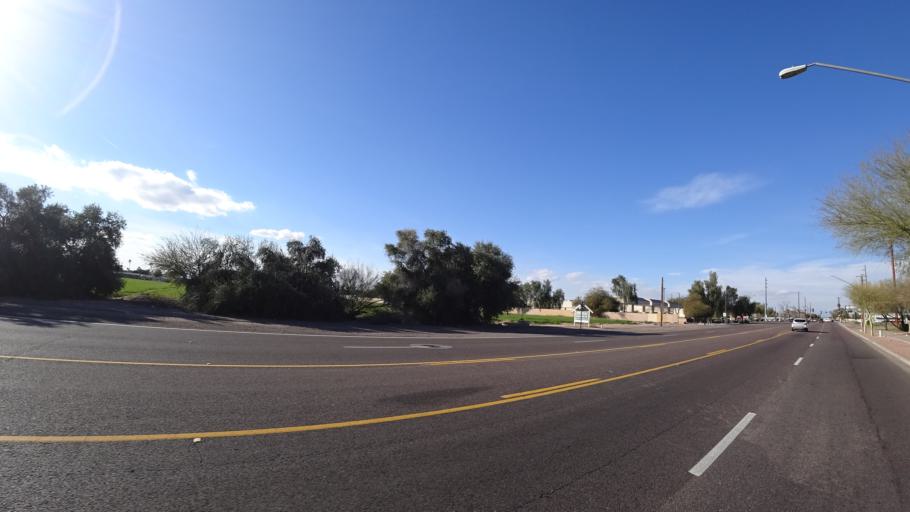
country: US
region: Arizona
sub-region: Maricopa County
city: Peoria
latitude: 33.5349
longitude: -112.2376
